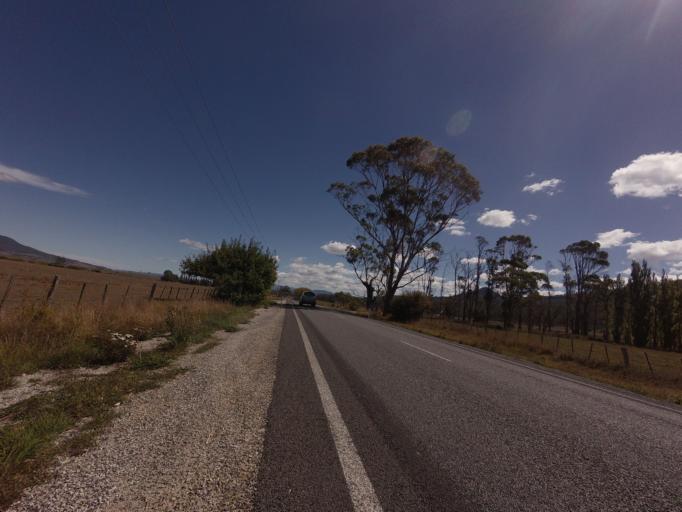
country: AU
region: Tasmania
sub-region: Break O'Day
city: St Helens
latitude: -41.5764
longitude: 148.1182
